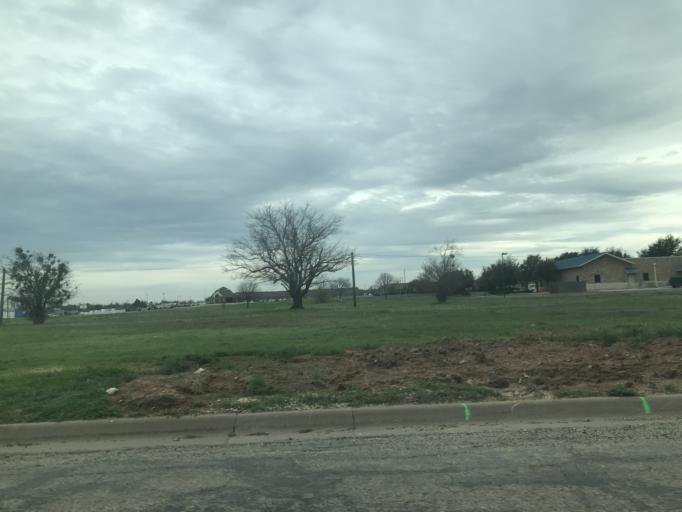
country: US
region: Texas
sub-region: Taylor County
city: Abilene
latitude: 32.4716
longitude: -99.7274
